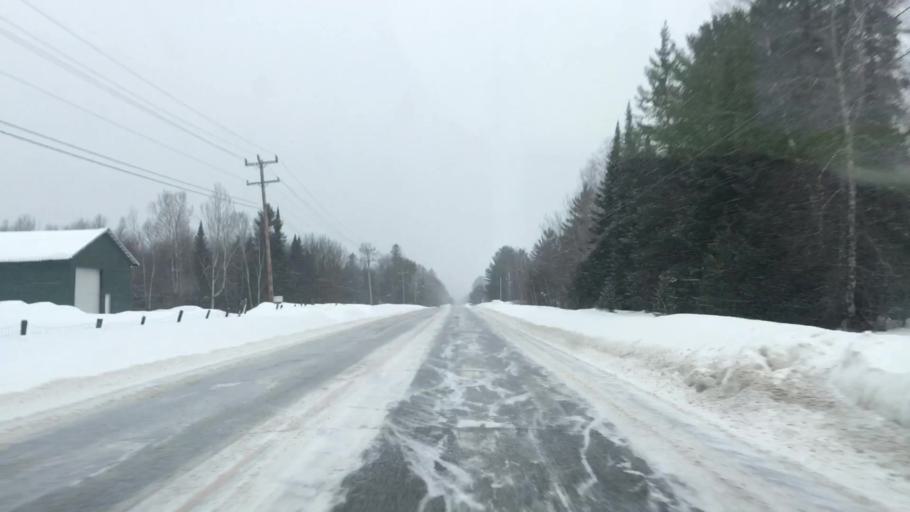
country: US
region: Maine
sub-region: Penobscot County
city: Medway
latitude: 45.5442
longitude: -68.3715
